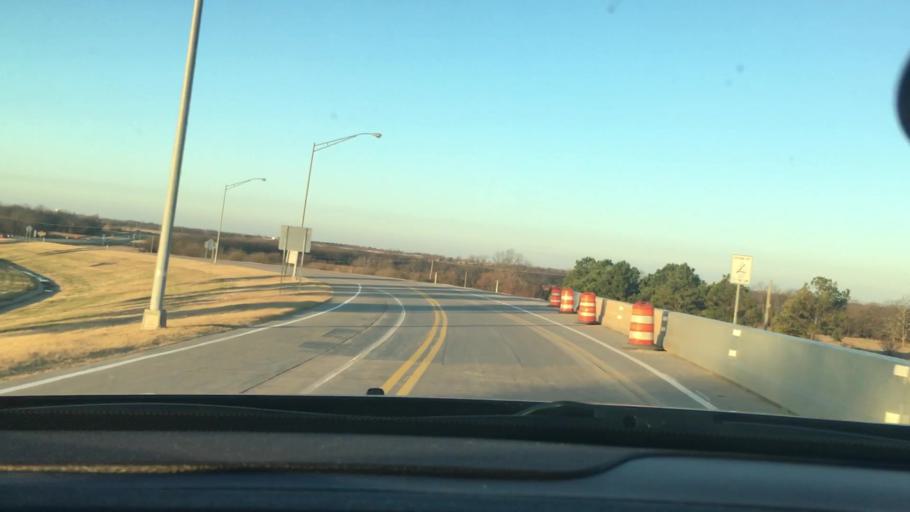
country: US
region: Oklahoma
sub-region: Pontotoc County
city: Ada
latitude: 34.6570
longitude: -96.7967
